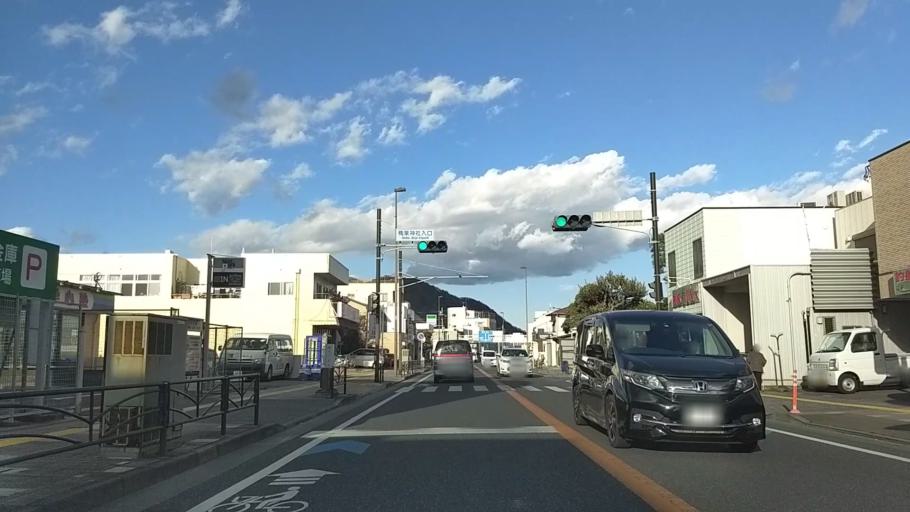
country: JP
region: Kanagawa
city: Oiso
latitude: 35.3097
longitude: 139.3156
